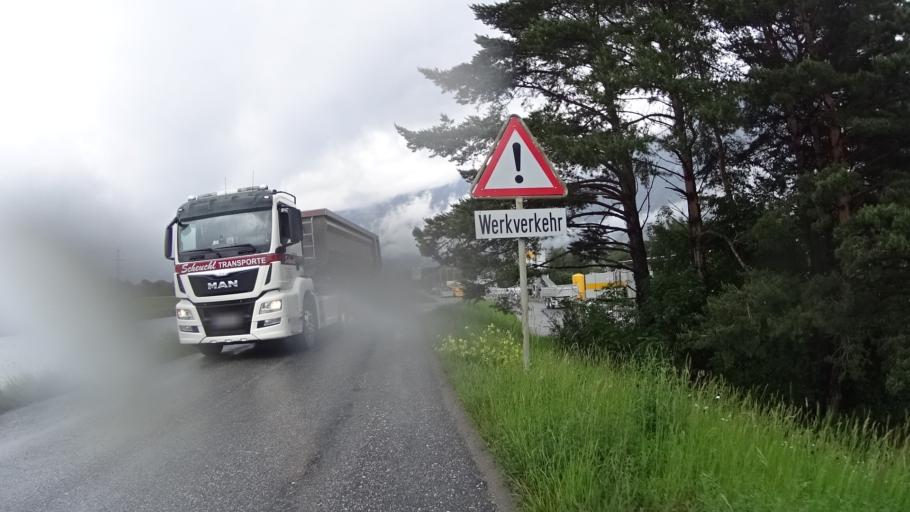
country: LI
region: Balzers
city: Balzers
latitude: 47.0754
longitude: 9.4966
